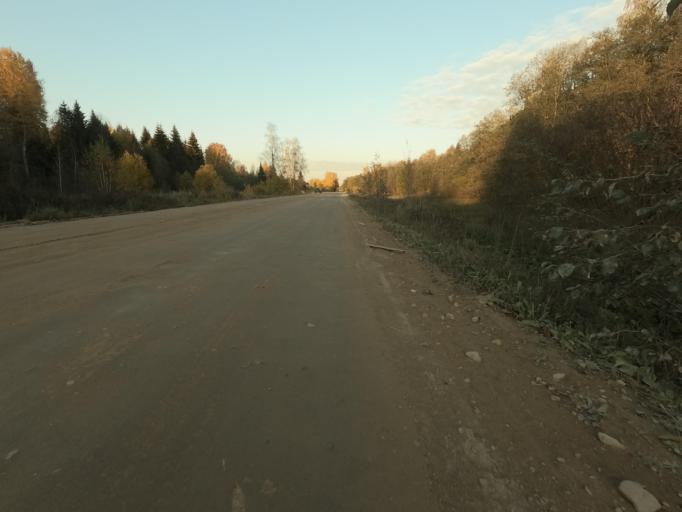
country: RU
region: Leningrad
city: Lyuban'
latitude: 59.0196
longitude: 31.0914
